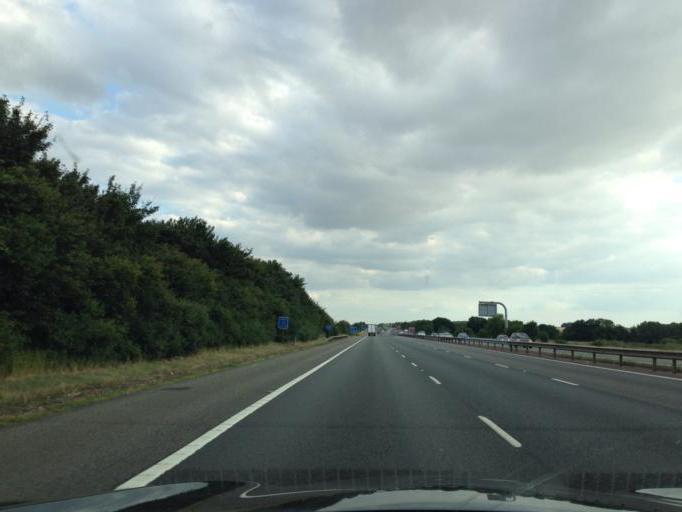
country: GB
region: England
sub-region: Oxfordshire
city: Banbury
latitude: 52.0589
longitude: -1.3073
